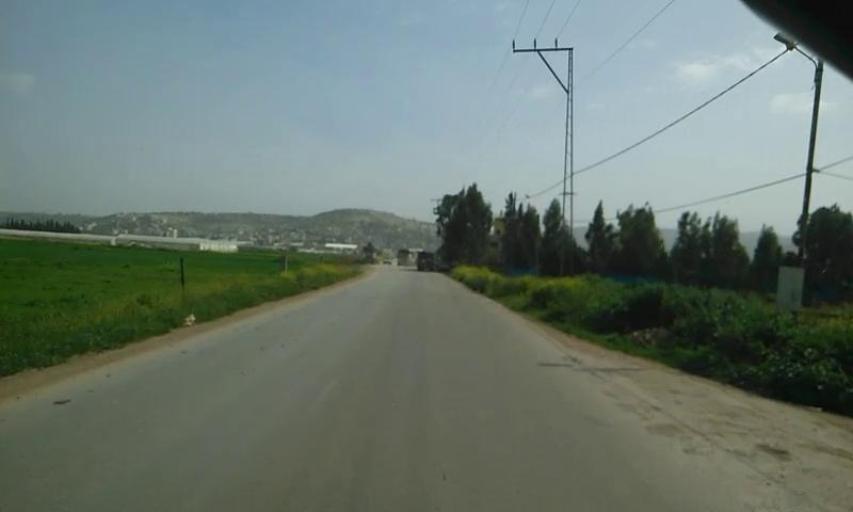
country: PS
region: West Bank
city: Ash Shuhada'
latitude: 32.4393
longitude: 35.2640
